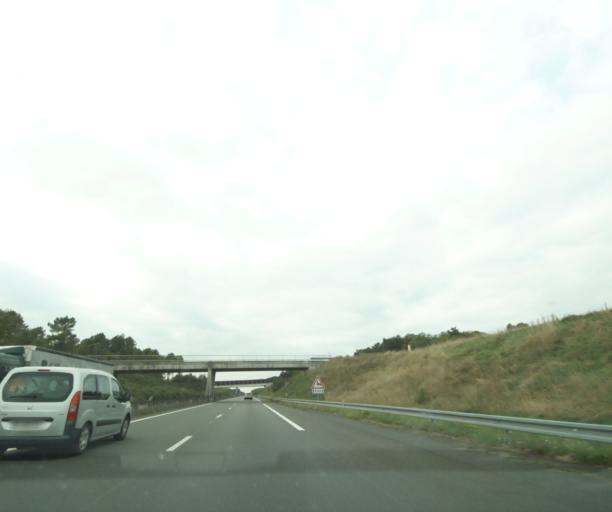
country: FR
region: Pays de la Loire
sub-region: Departement de la Sarthe
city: Luceau
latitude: 47.6944
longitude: 0.3597
